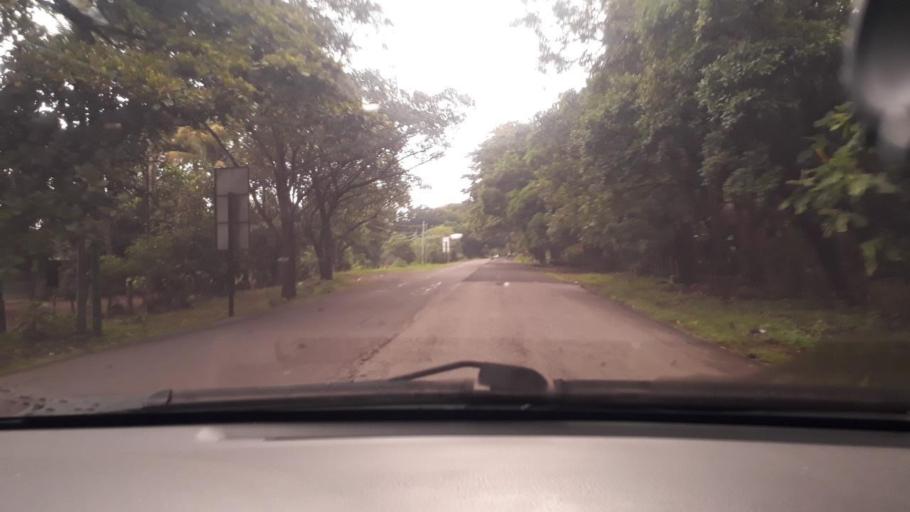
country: GT
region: Jutiapa
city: Jalpatagua
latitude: 14.1268
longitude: -89.9935
